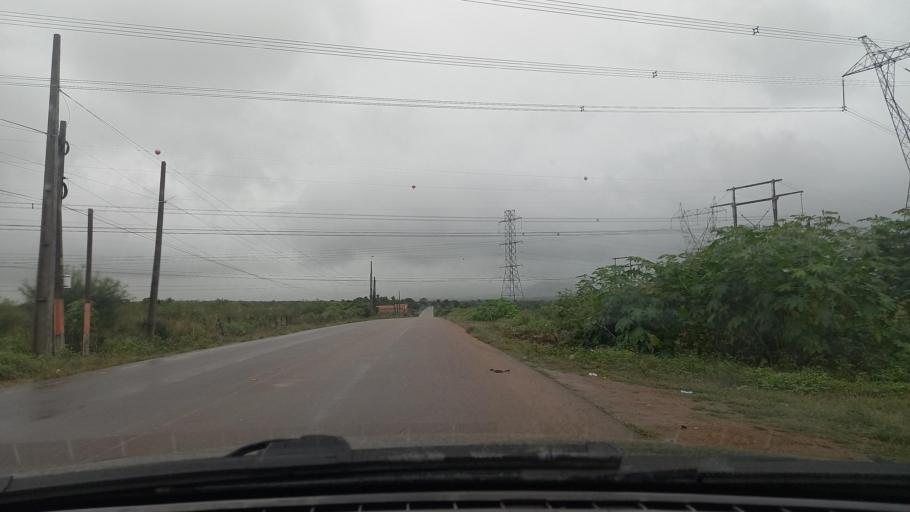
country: BR
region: Alagoas
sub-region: Delmiro Gouveia
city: Delmiro Gouveia
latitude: -9.3284
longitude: -37.9830
